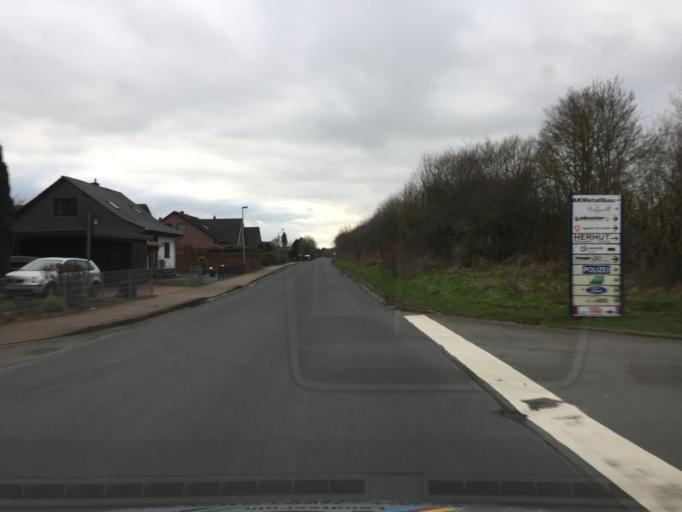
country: DE
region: Lower Saxony
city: Stolzenau
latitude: 52.5229
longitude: 9.0727
